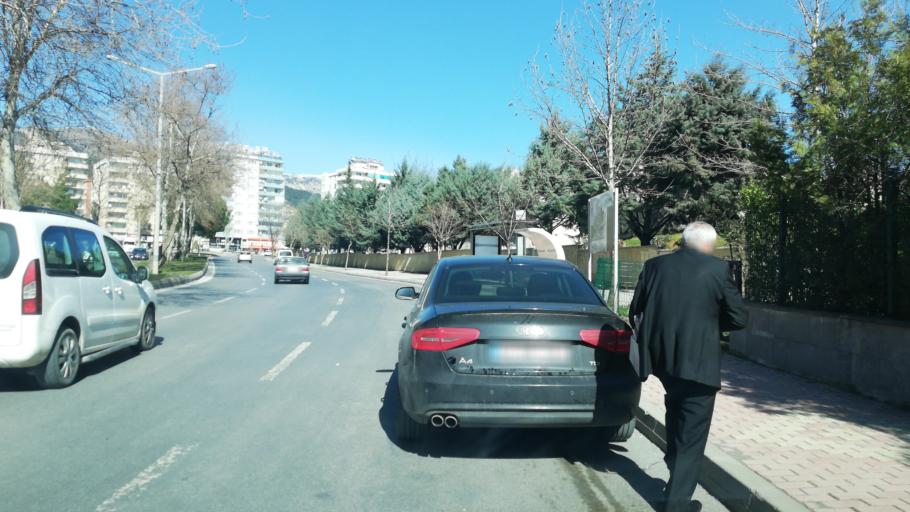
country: TR
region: Kahramanmaras
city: Kahramanmaras
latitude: 37.5848
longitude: 36.8972
